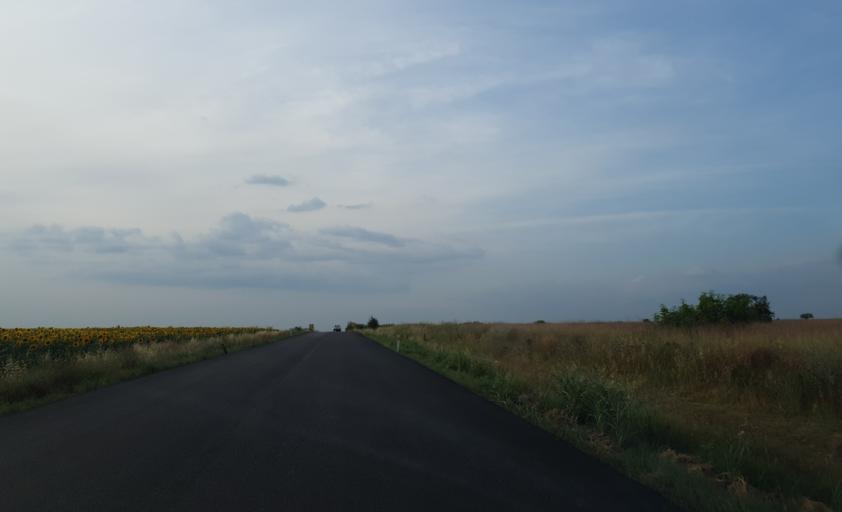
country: TR
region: Tekirdag
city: Hayrabolu
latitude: 41.3168
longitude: 27.1385
